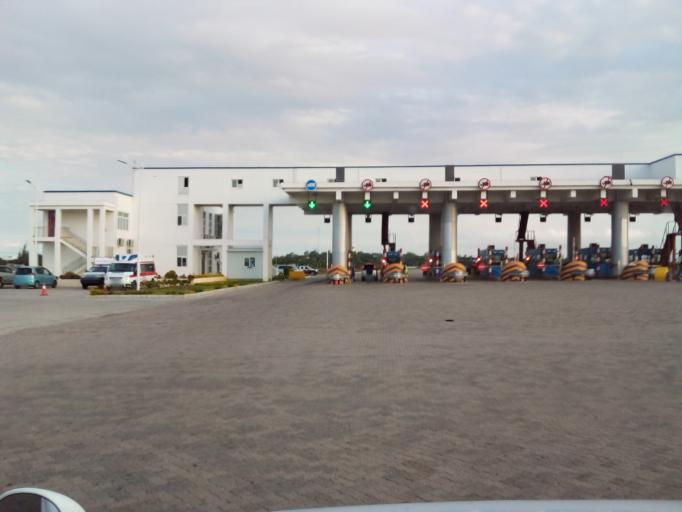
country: MZ
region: Maputo City
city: Maputo
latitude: -25.9955
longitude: 32.5558
